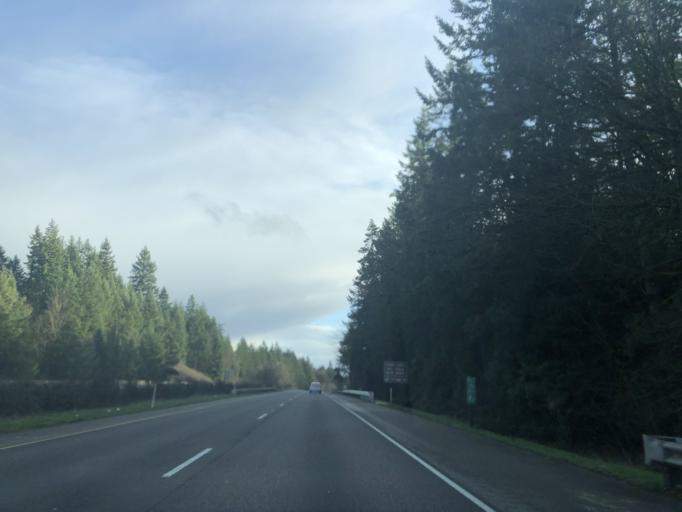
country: US
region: Washington
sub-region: Kitsap County
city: Bethel
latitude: 47.5126
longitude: -122.6539
